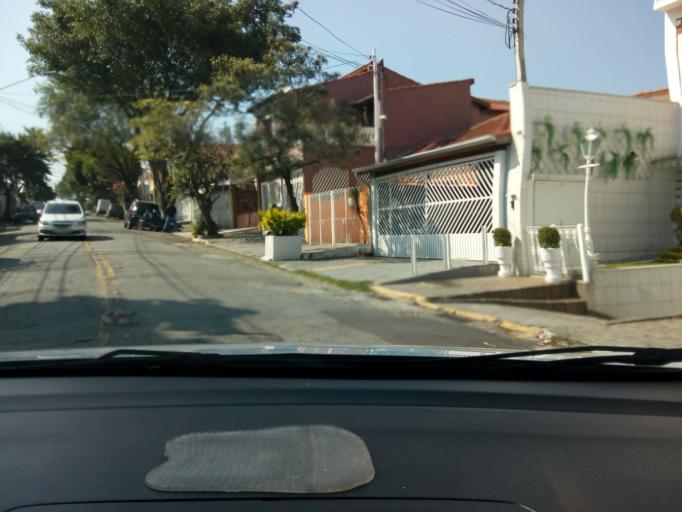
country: BR
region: Sao Paulo
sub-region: Sao Paulo
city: Sao Paulo
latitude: -23.5852
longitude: -46.6258
